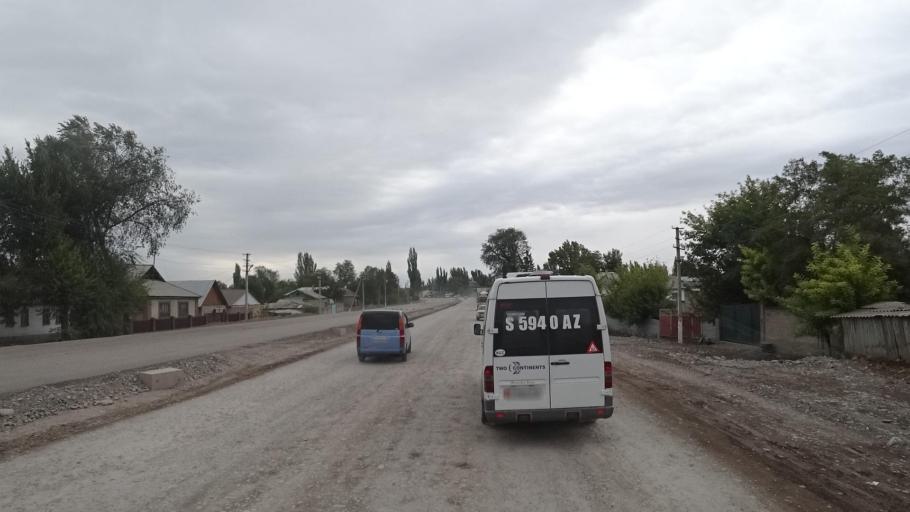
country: KG
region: Chuy
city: Belovodskoye
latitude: 42.8344
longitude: 74.1264
